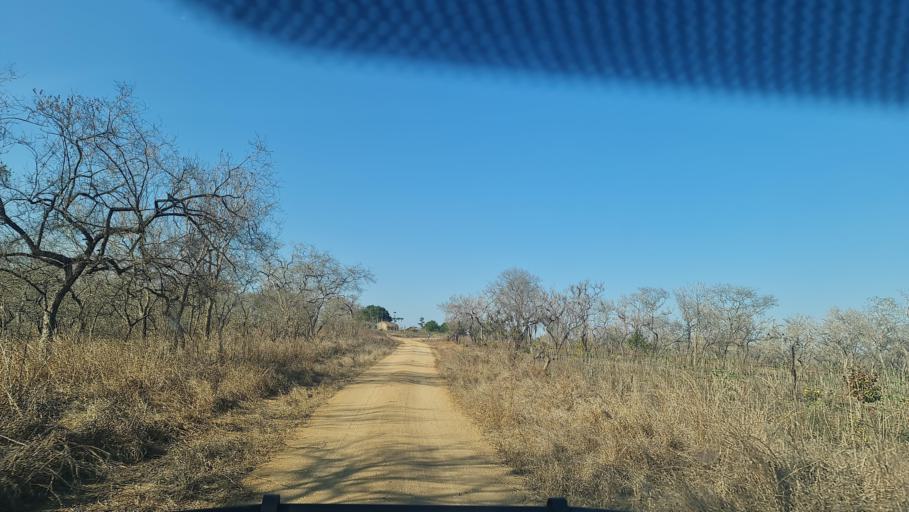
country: MZ
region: Nampula
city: Nacala
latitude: -13.9458
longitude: 40.4796
